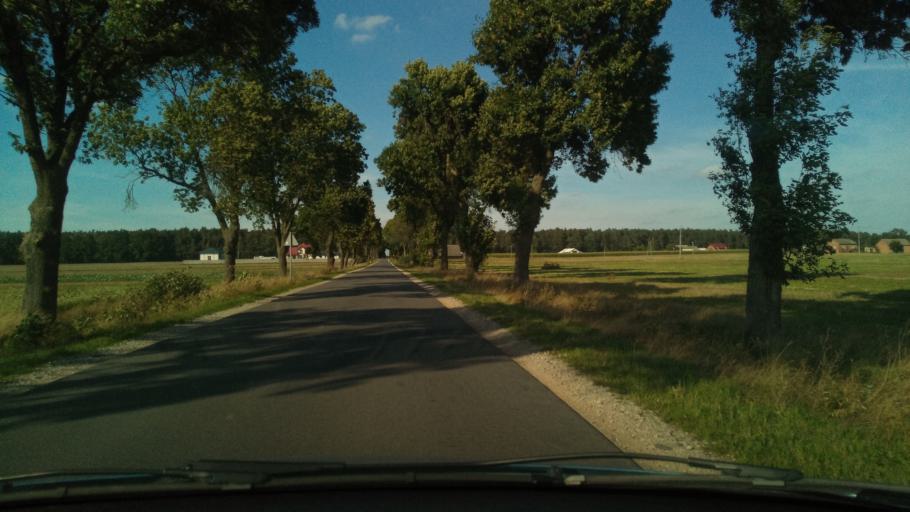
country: PL
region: Lodz Voivodeship
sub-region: Powiat piotrkowski
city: Sulejow
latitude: 51.4028
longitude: 19.8242
